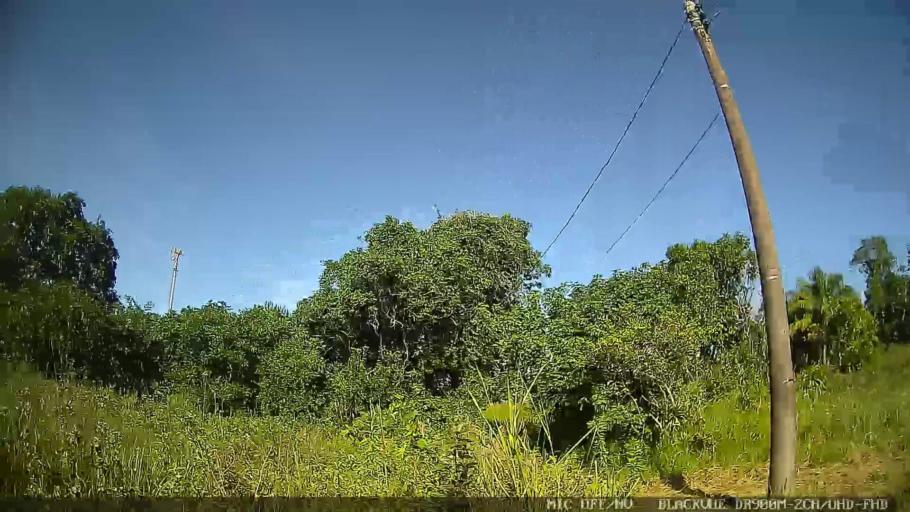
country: BR
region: Sao Paulo
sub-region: Itanhaem
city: Itanhaem
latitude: -24.2218
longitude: -46.8779
